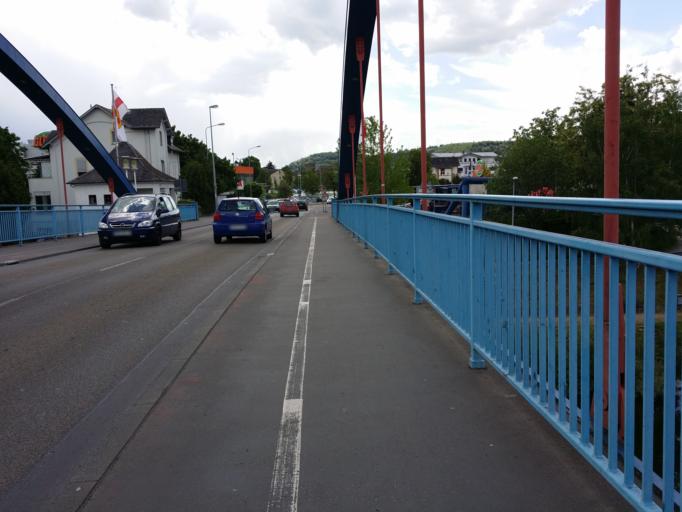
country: DE
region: Rheinland-Pfalz
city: Lahnstein
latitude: 50.3084
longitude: 7.6040
